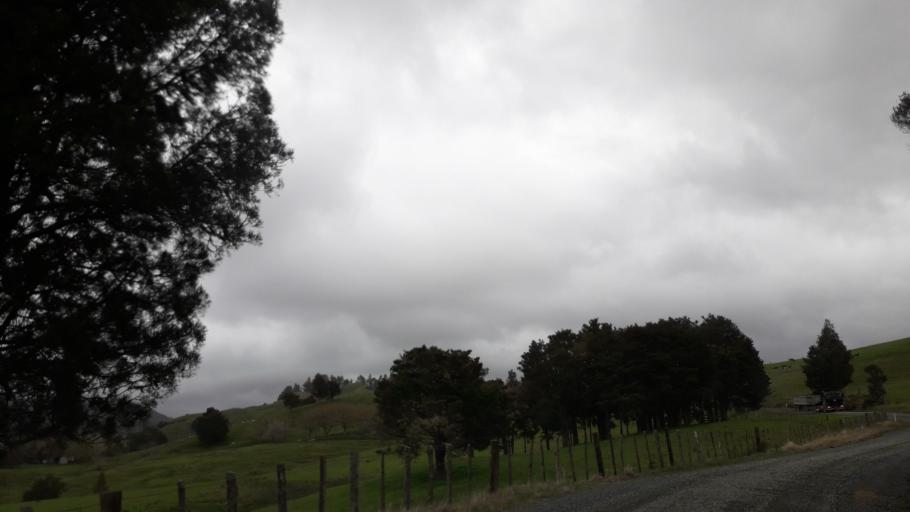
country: NZ
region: Northland
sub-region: Far North District
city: Waimate North
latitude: -35.1377
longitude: 173.7129
